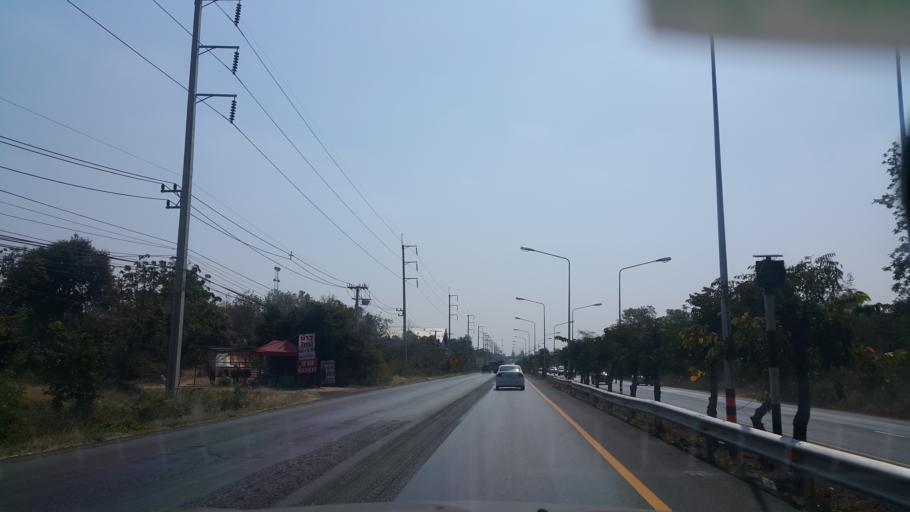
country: TH
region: Nakhon Ratchasima
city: Sida
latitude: 15.5555
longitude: 102.5500
